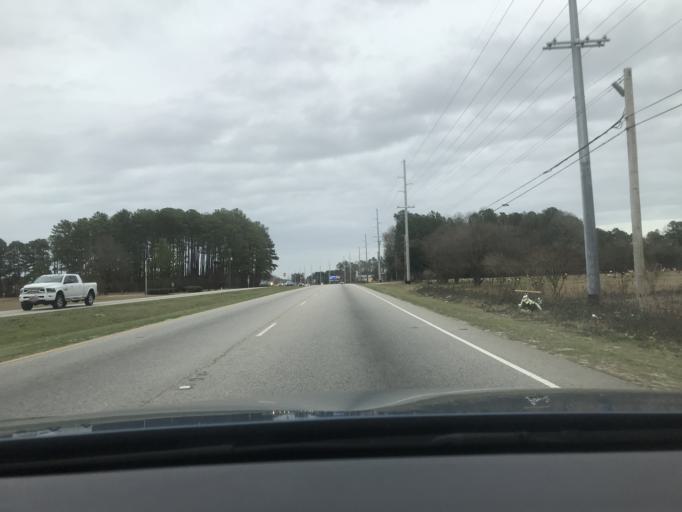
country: US
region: North Carolina
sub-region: Hoke County
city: Rockfish
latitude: 35.0381
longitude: -79.0048
